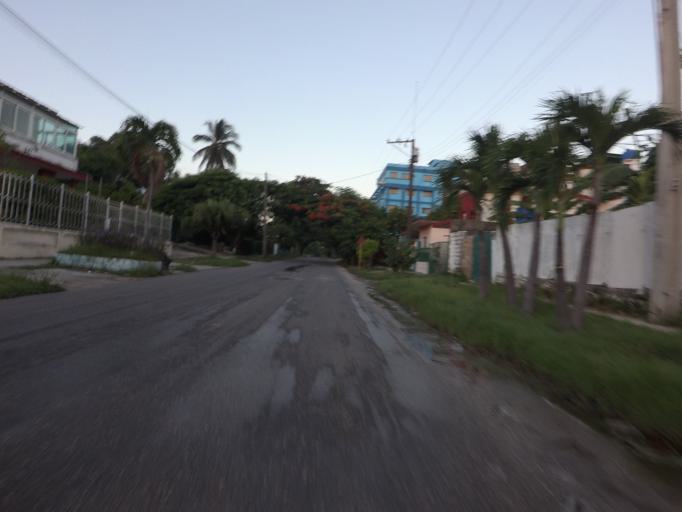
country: CU
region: La Habana
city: Havana
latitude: 23.1235
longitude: -82.3905
